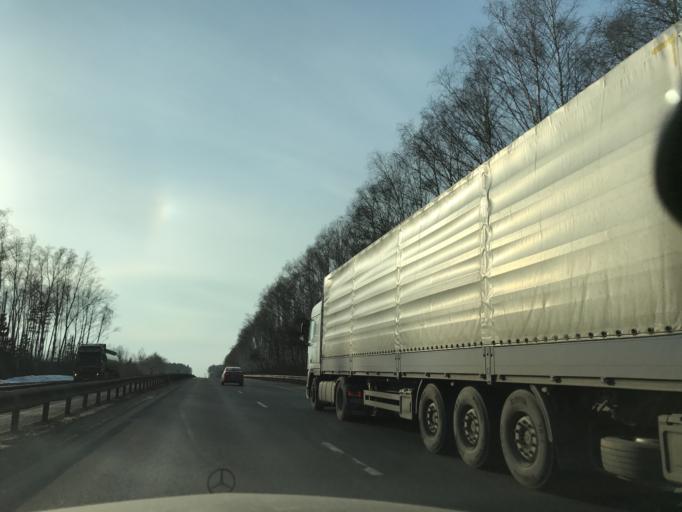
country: RU
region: Vladimir
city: Melekhovo
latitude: 56.2086
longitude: 41.2477
